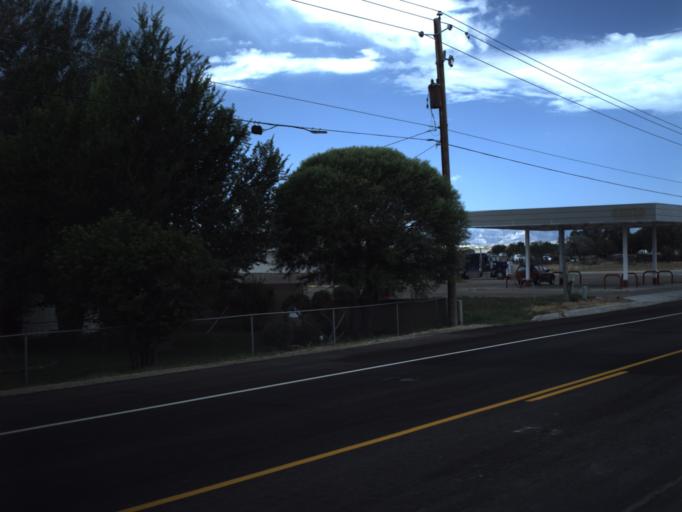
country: US
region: Utah
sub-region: Carbon County
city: Wellington
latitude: 39.5425
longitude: -110.7144
